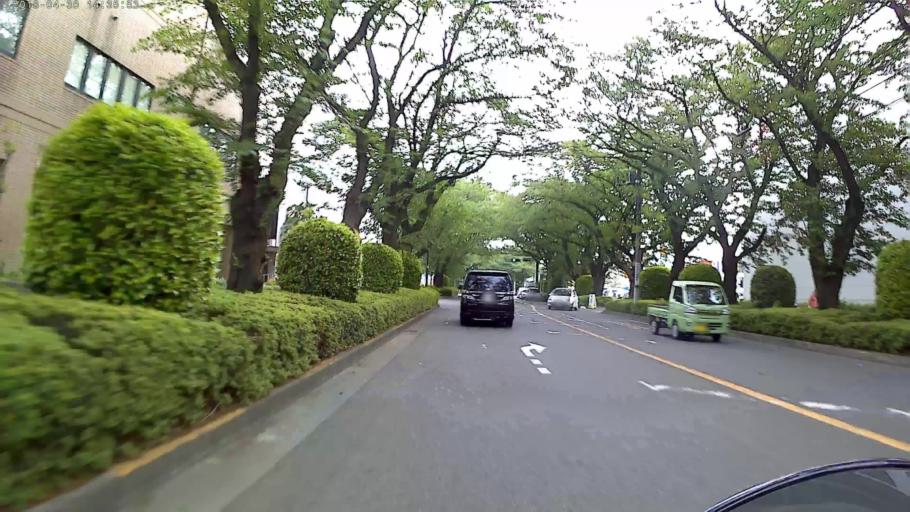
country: JP
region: Kanagawa
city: Zama
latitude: 35.5731
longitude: 139.3704
